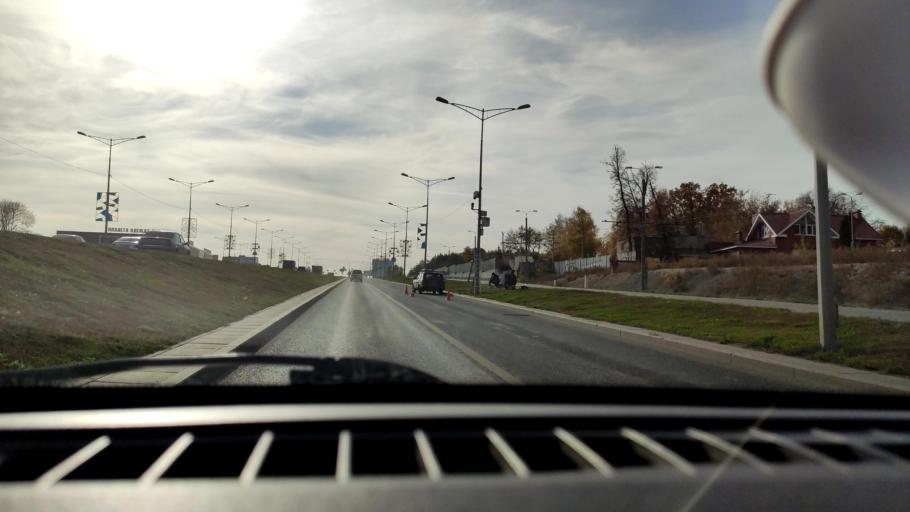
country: RU
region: Samara
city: Samara
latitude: 53.2665
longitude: 50.2484
